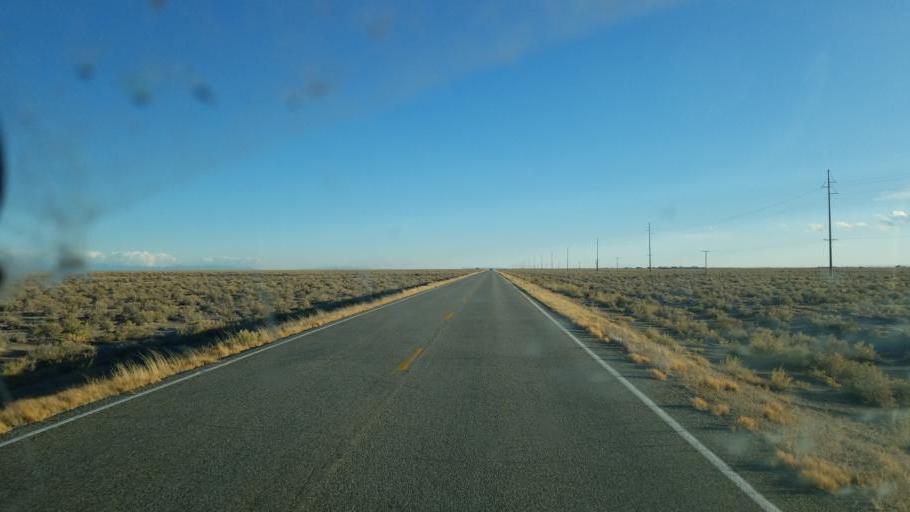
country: US
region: Colorado
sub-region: Saguache County
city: Center
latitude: 37.8718
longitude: -105.8944
